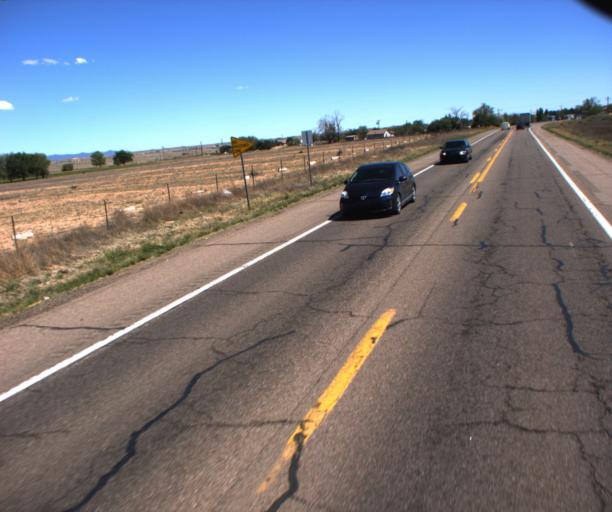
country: US
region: Arizona
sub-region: Yavapai County
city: Chino Valley
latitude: 34.8075
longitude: -112.4511
